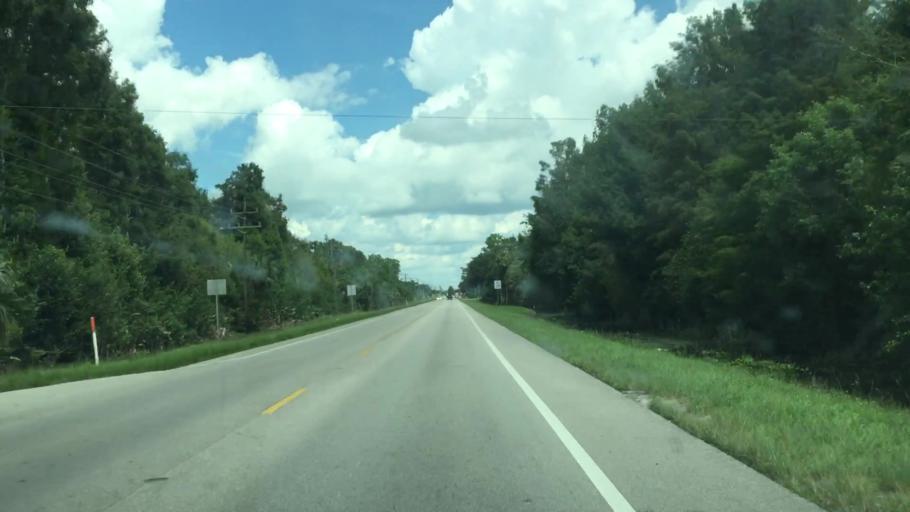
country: US
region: Florida
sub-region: Collier County
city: Immokalee
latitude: 26.4041
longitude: -81.4171
